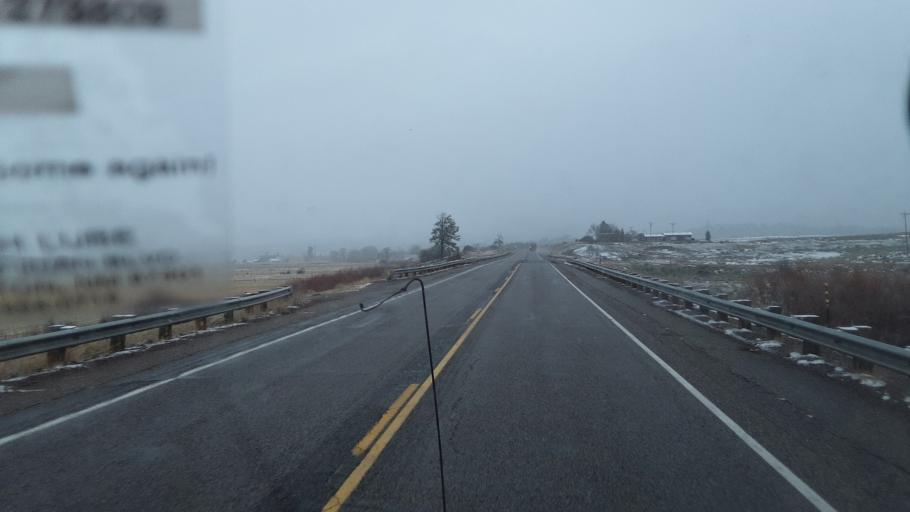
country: US
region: New Mexico
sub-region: Rio Arriba County
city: Tierra Amarilla
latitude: 36.7536
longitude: -106.5623
